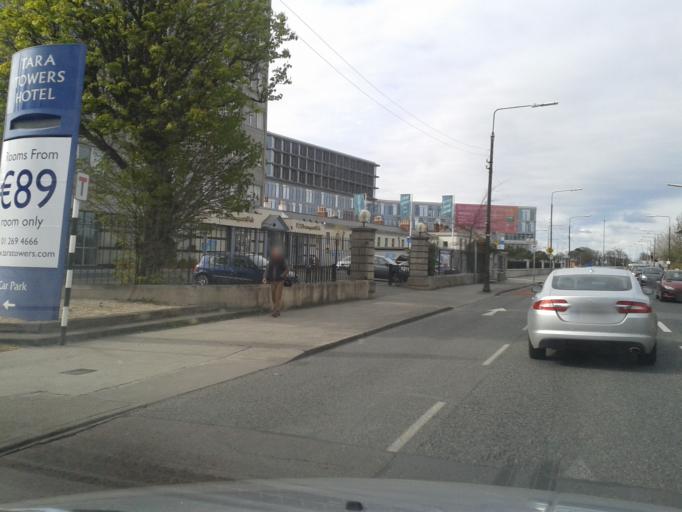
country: IE
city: Booterstown
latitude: 53.3123
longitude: -6.2015
